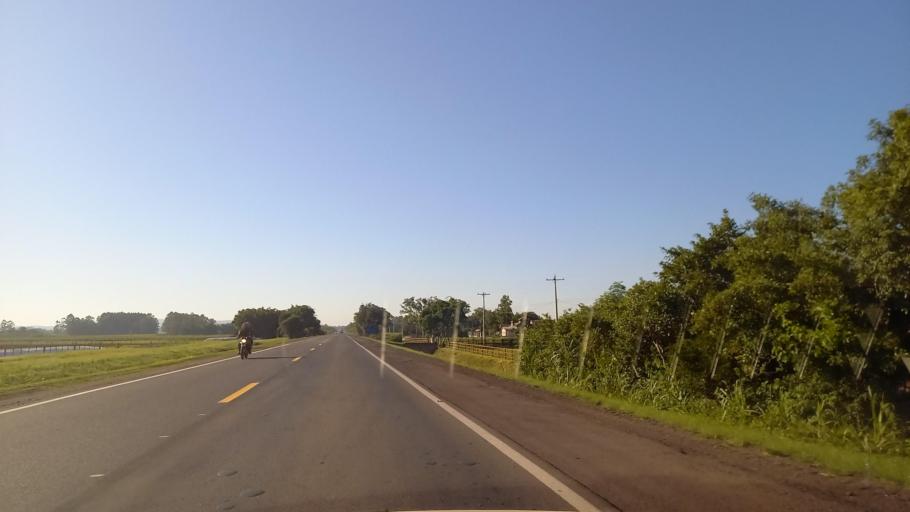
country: BR
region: Rio Grande do Sul
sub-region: Venancio Aires
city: Venancio Aires
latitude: -29.6615
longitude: -52.0676
